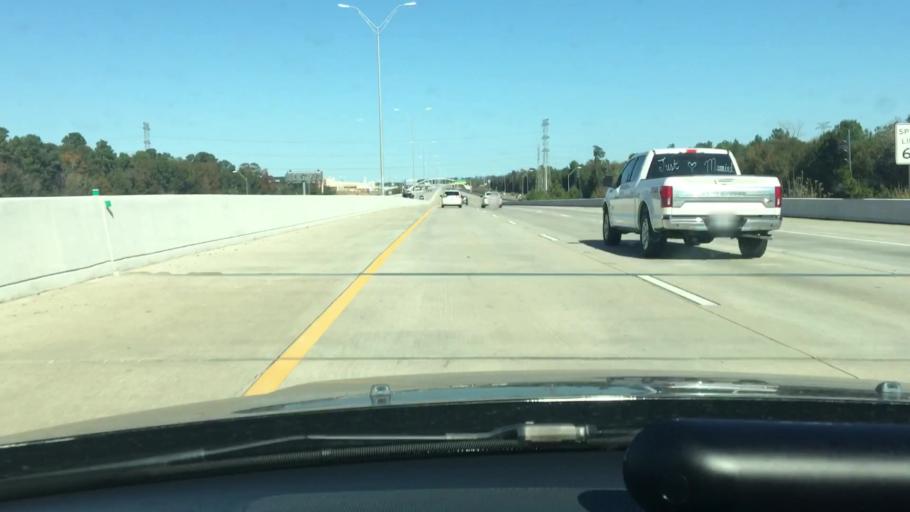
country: US
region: Texas
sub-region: Harris County
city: Sheldon
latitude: 29.9073
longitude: -95.2021
